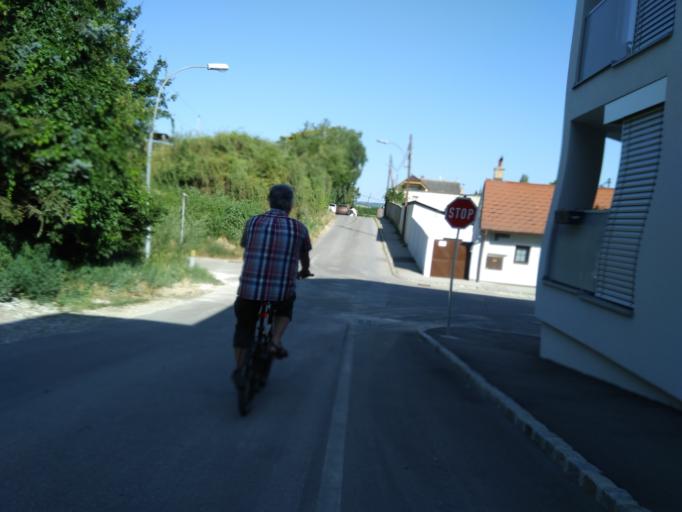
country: AT
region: Lower Austria
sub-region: Politischer Bezirk Mistelbach
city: Wolkersdorf im Weinviertel
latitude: 48.3828
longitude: 16.5097
